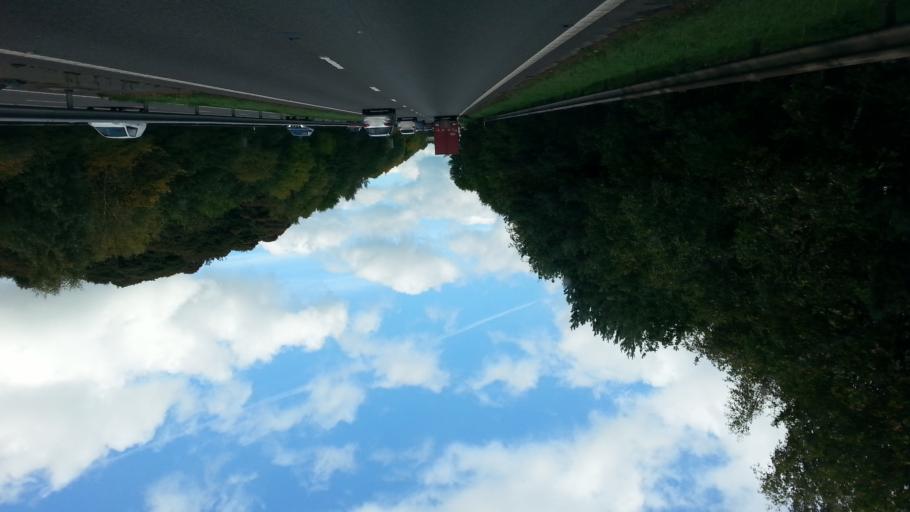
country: GB
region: England
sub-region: Derbyshire
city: Little Eaton
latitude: 52.9638
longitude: -1.4561
